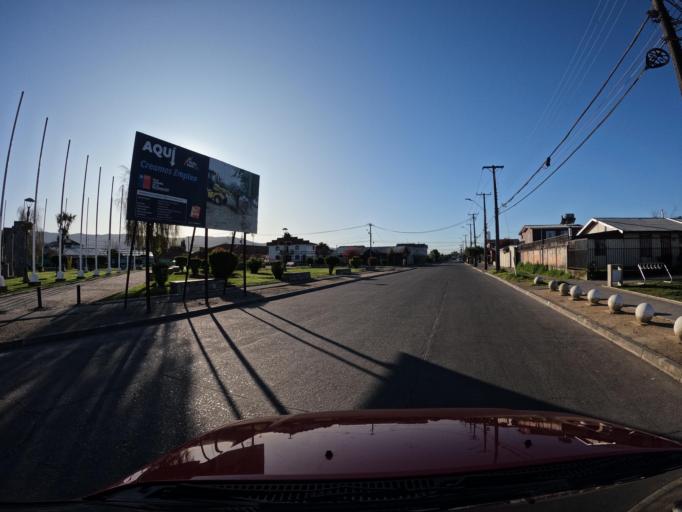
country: CL
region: Biobio
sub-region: Provincia de Concepcion
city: Chiguayante
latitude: -36.9298
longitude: -73.0262
